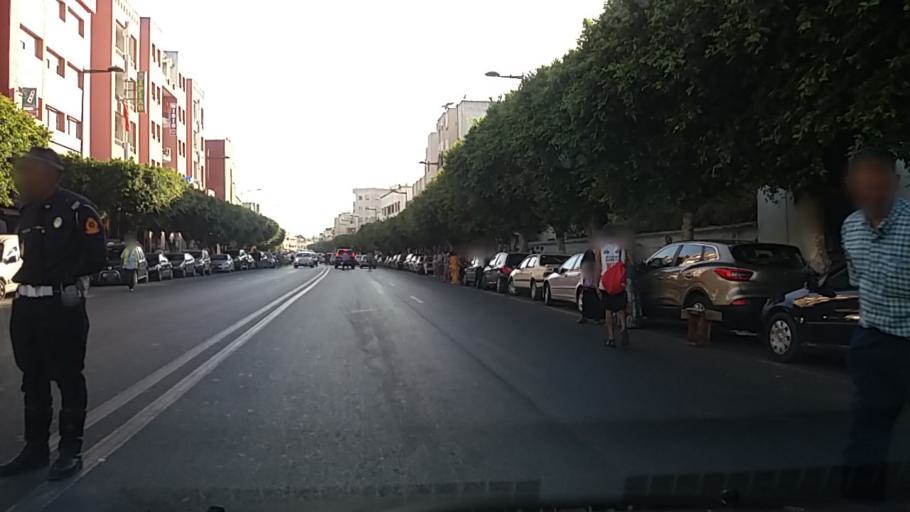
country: MA
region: Gharb-Chrarda-Beni Hssen
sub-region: Kenitra Province
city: Kenitra
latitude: 34.2655
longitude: -6.5649
